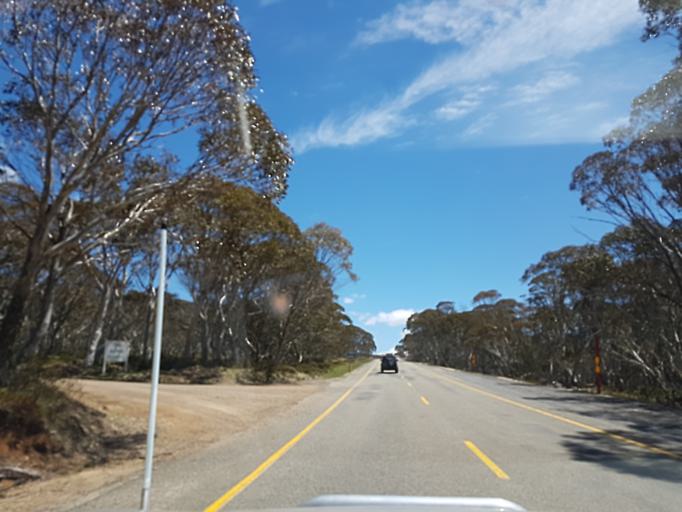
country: AU
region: Victoria
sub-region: Alpine
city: Mount Beauty
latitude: -37.0227
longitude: 147.2473
